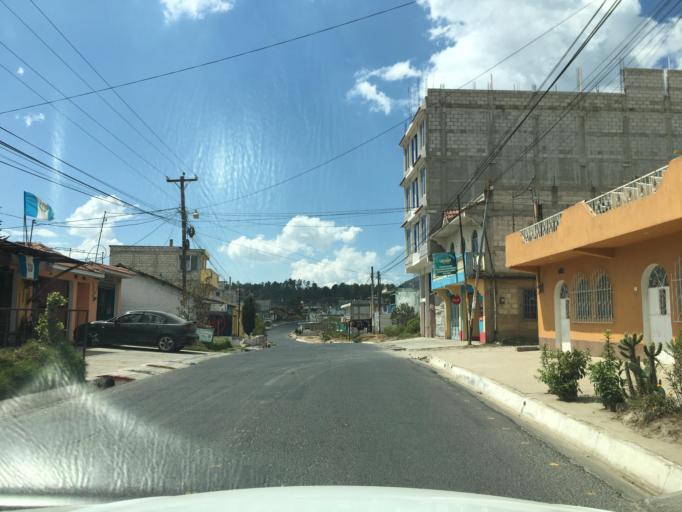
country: GT
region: Totonicapan
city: San Cristobal Totonicapan
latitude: 14.9077
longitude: -91.4536
